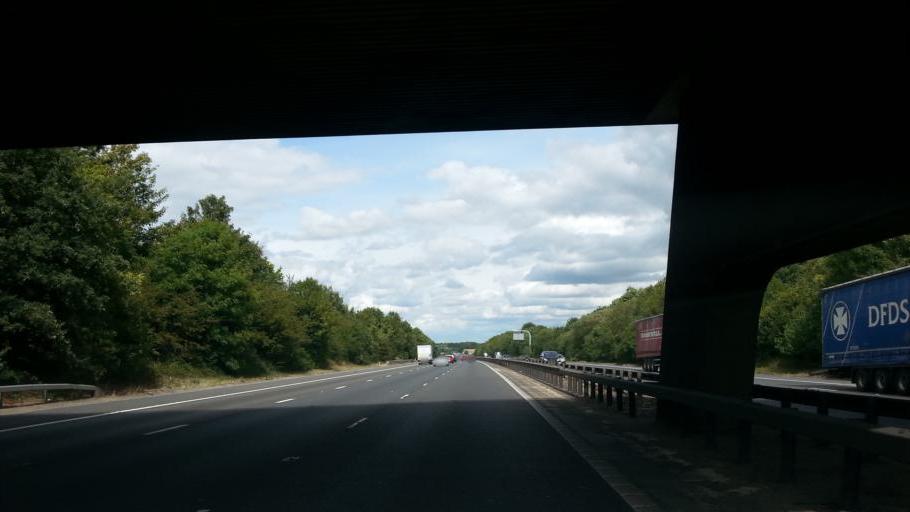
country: GB
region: England
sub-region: Hertfordshire
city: Sawbridgeworth
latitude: 51.7826
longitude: 0.1678
